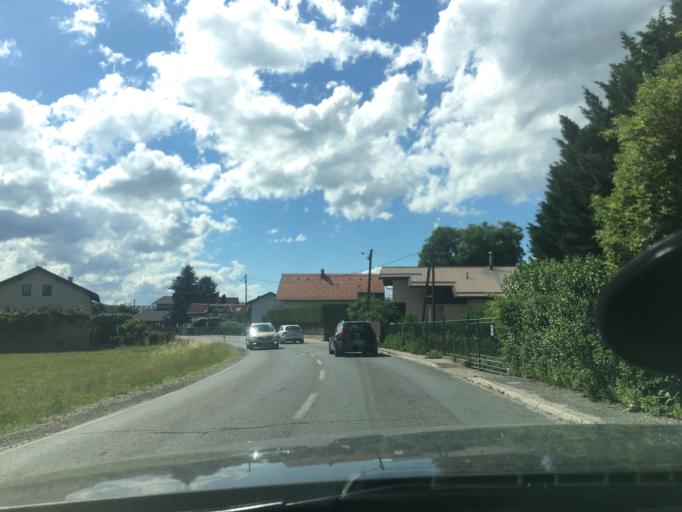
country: SI
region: Maribor
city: Razvanje
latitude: 46.5330
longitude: 15.6326
